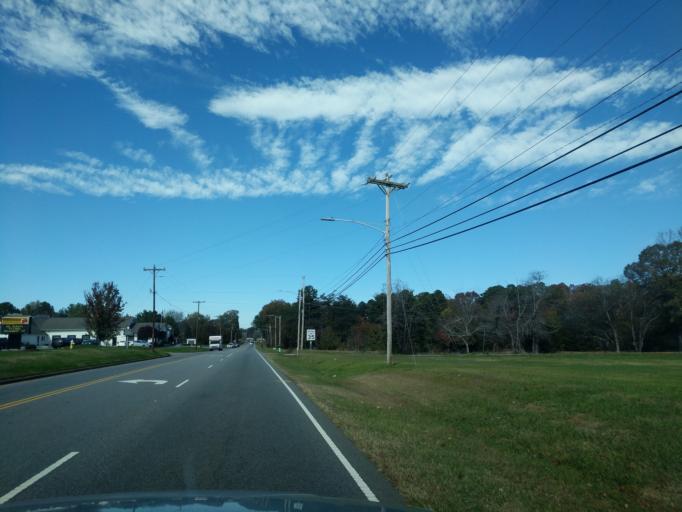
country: US
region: North Carolina
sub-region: Catawba County
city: Newton
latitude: 35.6363
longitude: -81.2675
